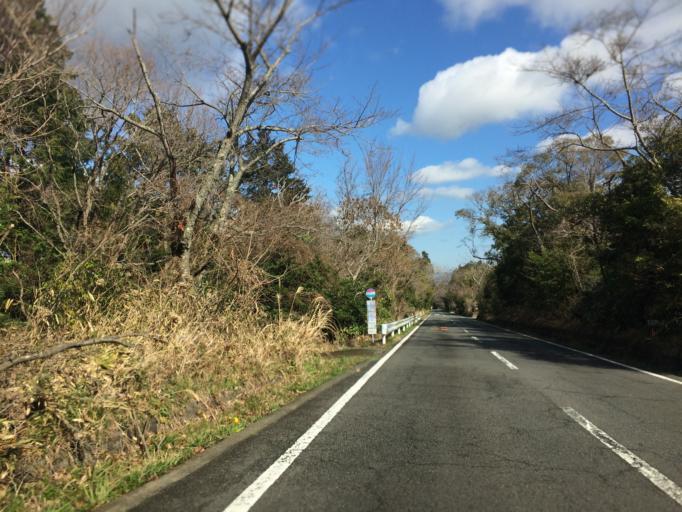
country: JP
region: Shizuoka
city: Shizuoka-shi
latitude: 34.9686
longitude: 138.4480
